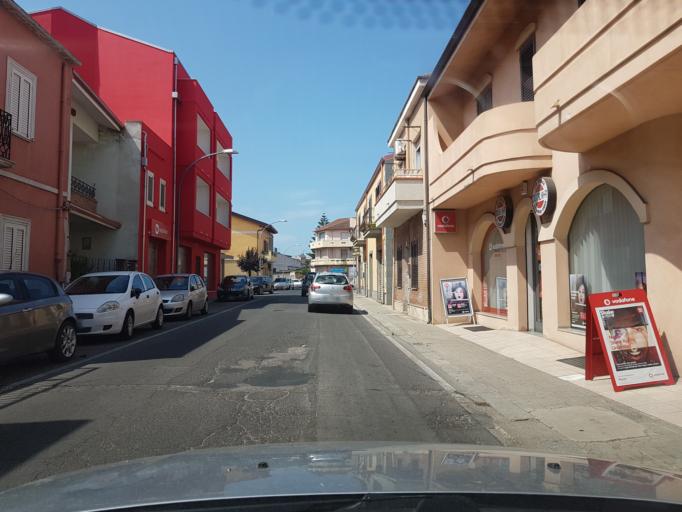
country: IT
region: Sardinia
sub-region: Provincia di Oristano
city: Oristano
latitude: 39.9069
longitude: 8.5985
